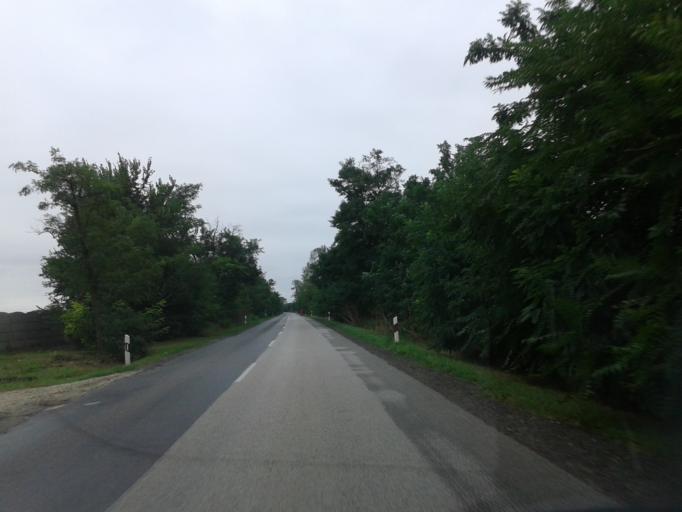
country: HU
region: Bacs-Kiskun
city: Dunavecse
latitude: 46.9499
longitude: 18.9792
